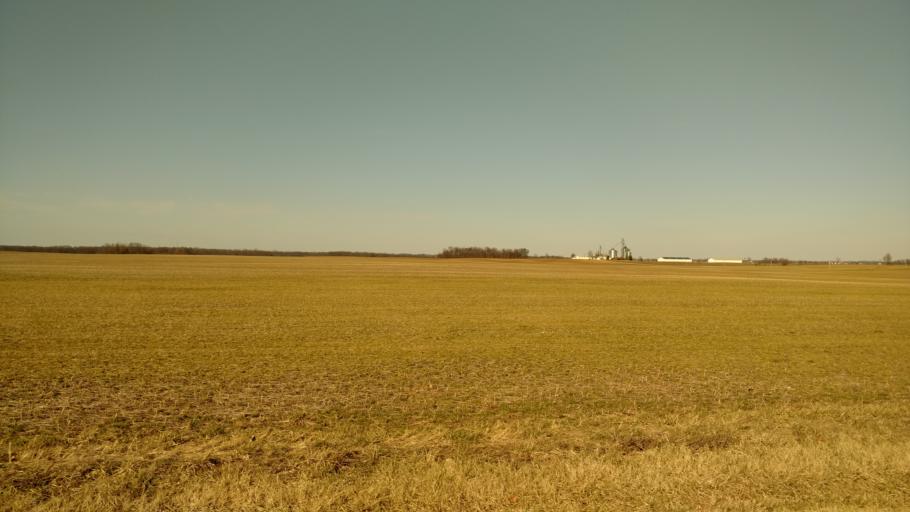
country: US
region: Ohio
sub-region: Marion County
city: Marion
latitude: 40.7022
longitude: -83.2136
